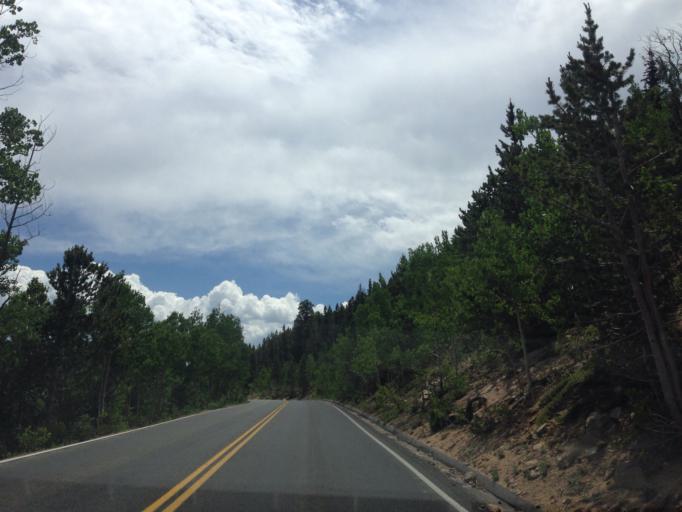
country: US
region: Colorado
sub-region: Larimer County
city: Estes Park
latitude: 40.3981
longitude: -105.6431
